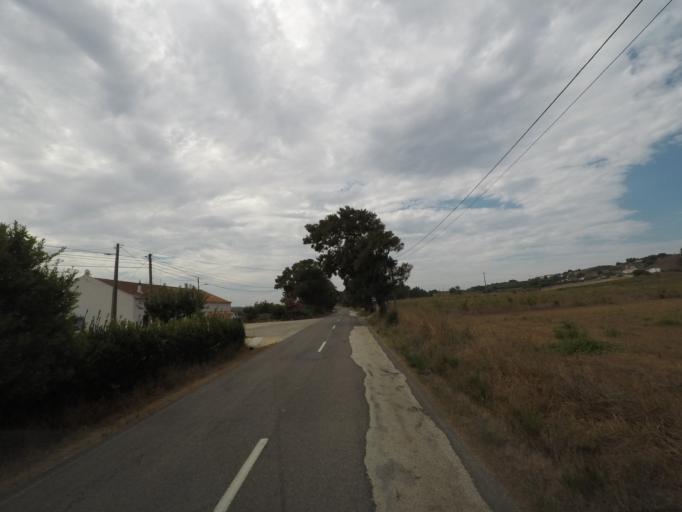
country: PT
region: Faro
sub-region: Aljezur
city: Aljezur
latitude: 37.2464
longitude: -8.8224
